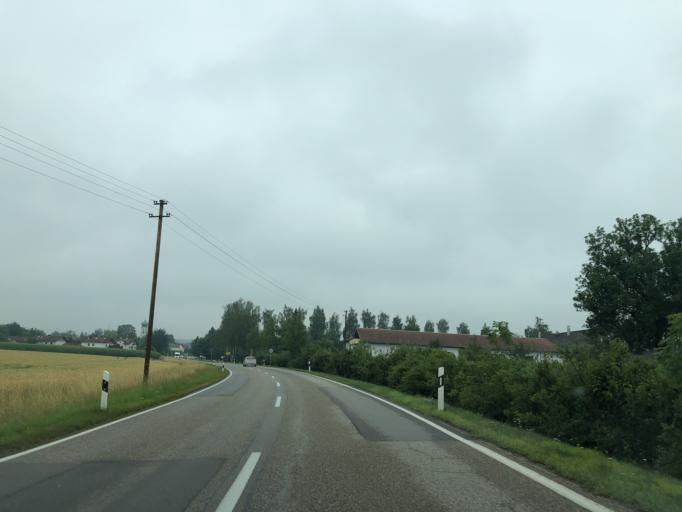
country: DE
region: Bavaria
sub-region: Upper Bavaria
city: Worth
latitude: 48.2475
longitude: 11.9341
